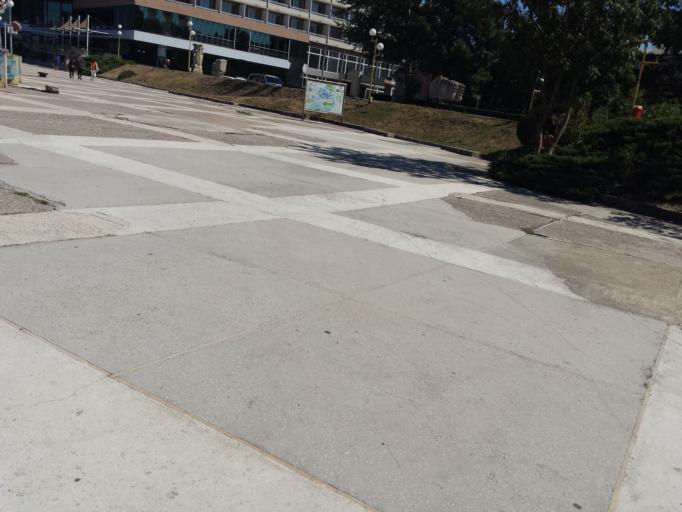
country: RO
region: Tulcea
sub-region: Municipiul Tulcea
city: Tulcea
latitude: 45.1798
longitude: 28.8023
